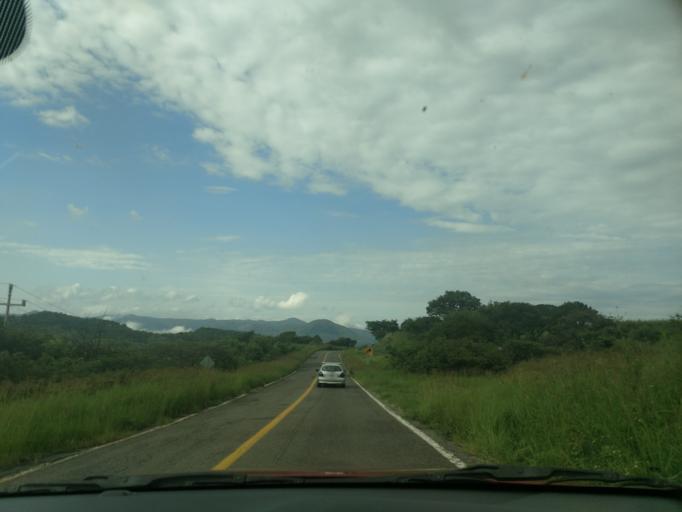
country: MX
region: Jalisco
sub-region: Atengo
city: Soyatlan del Oro
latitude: 20.5451
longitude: -104.2937
